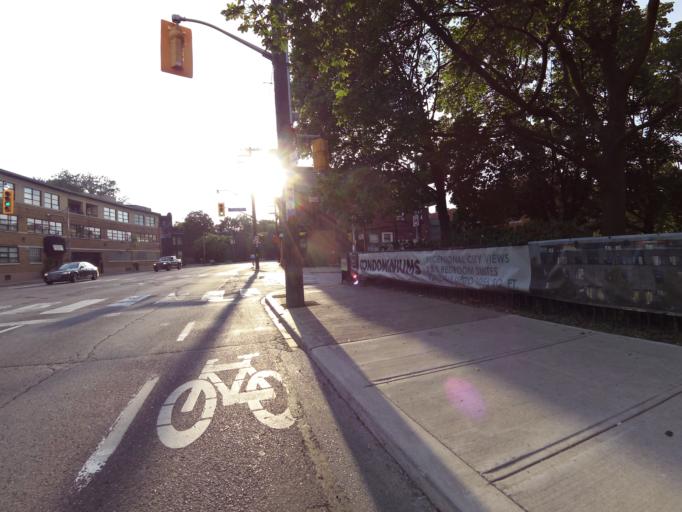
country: CA
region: Ontario
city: Toronto
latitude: 43.6744
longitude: -79.3995
